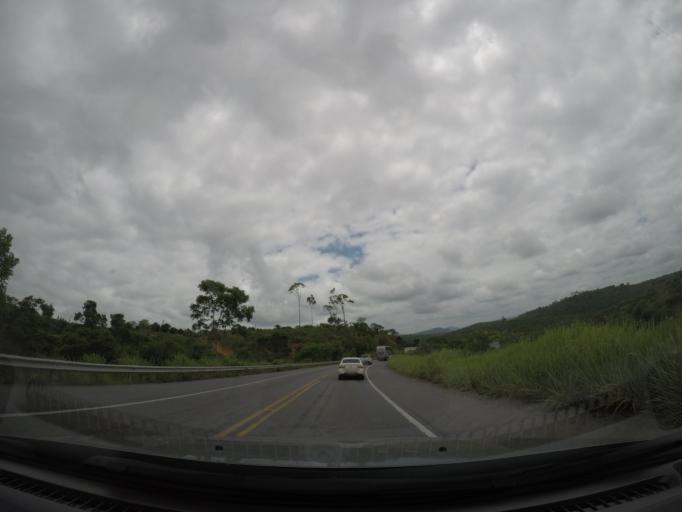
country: BR
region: Bahia
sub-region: Ruy Barbosa
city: Terra Nova
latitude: -12.4577
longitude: -40.5843
